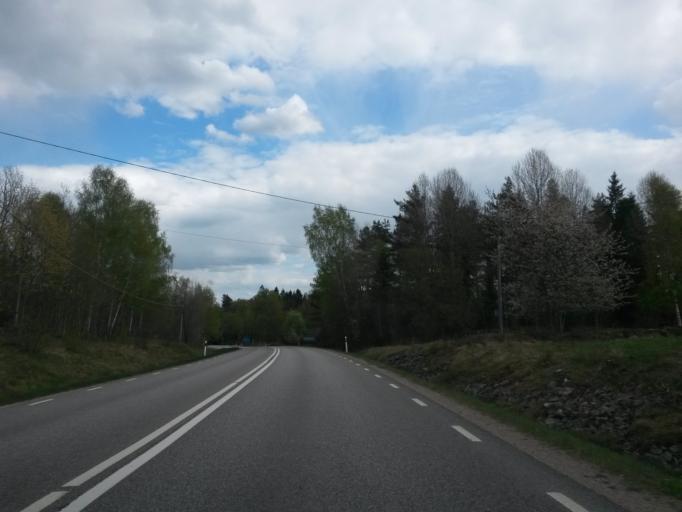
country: SE
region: Vaestra Goetaland
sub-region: Vargarda Kommun
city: Vargarda
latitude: 57.9481
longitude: 12.8271
